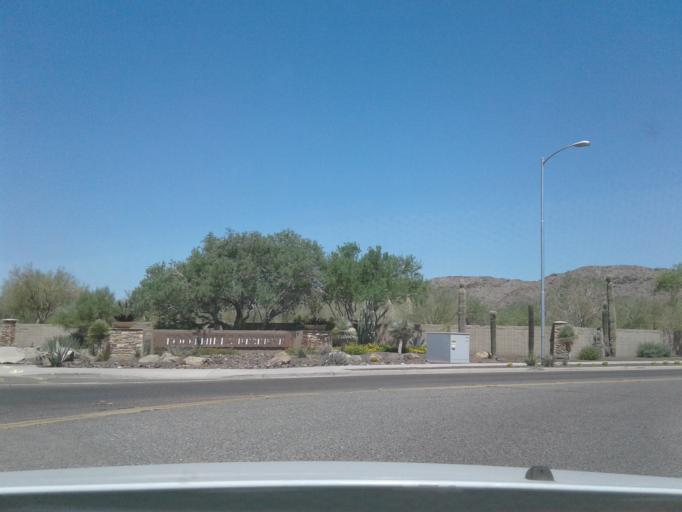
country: US
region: Arizona
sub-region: Maricopa County
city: Laveen
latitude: 33.2910
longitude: -112.1171
